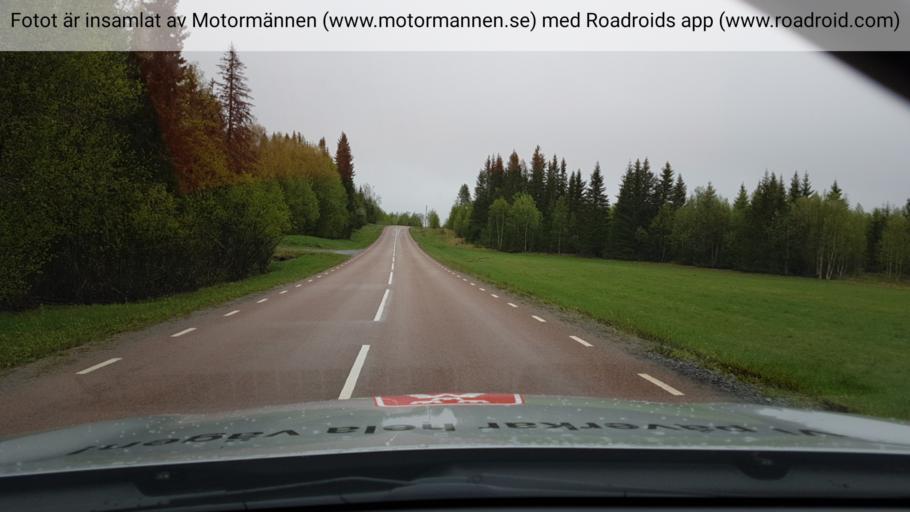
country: SE
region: Jaemtland
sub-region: Krokoms Kommun
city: Valla
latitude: 63.1648
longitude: 13.9919
